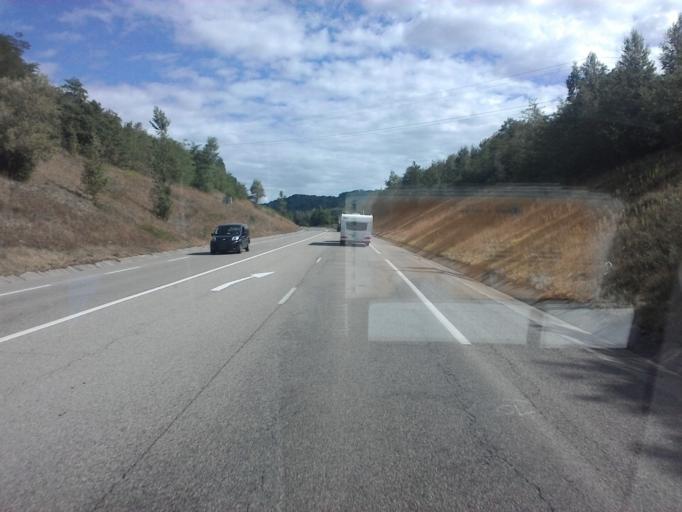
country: FR
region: Rhone-Alpes
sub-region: Departement de l'Ain
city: Vaux-en-Bugey
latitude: 45.9174
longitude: 5.3388
